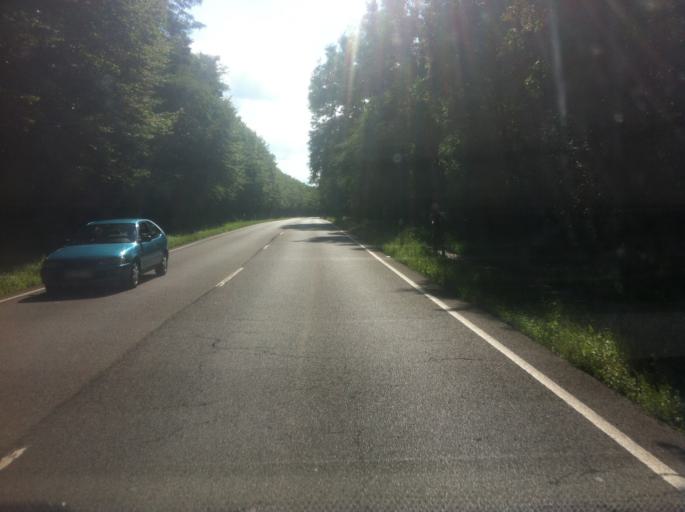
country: DE
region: North Rhine-Westphalia
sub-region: Regierungsbezirk Koln
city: Hurth
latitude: 50.8354
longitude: 6.8630
